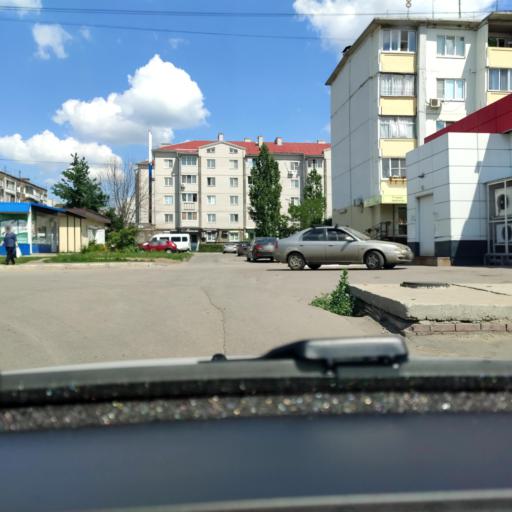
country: RU
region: Voronezj
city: Semiluki
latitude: 51.6940
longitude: 39.0097
